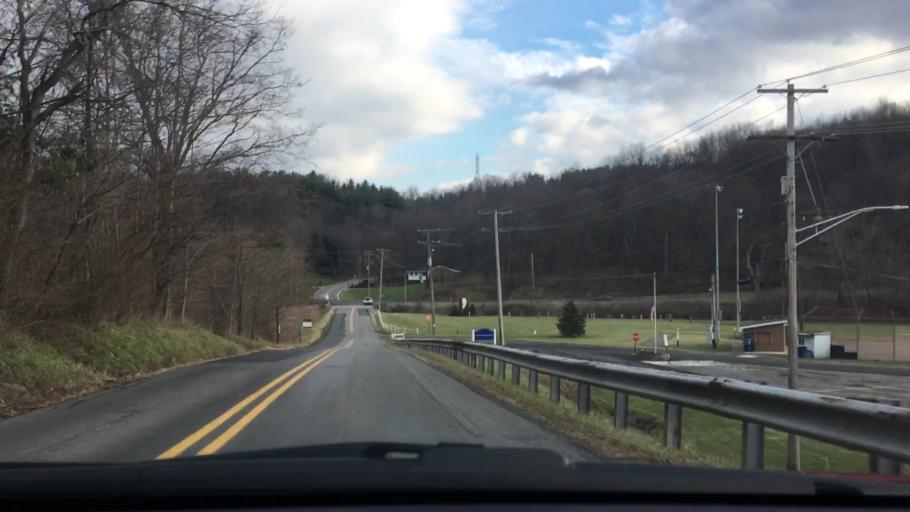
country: US
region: Pennsylvania
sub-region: Allegheny County
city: Sturgeon
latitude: 40.4173
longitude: -80.2230
